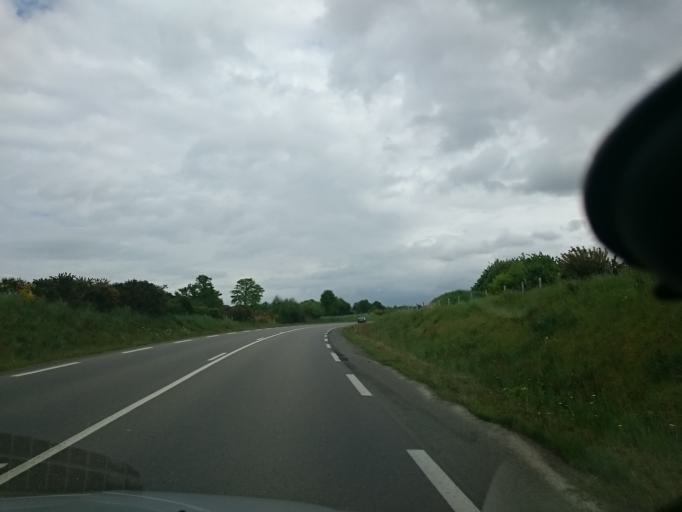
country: FR
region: Brittany
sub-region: Departement d'Ille-et-Vilaine
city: Saint-Etienne-en-Cogles
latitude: 48.3948
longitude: -1.3377
